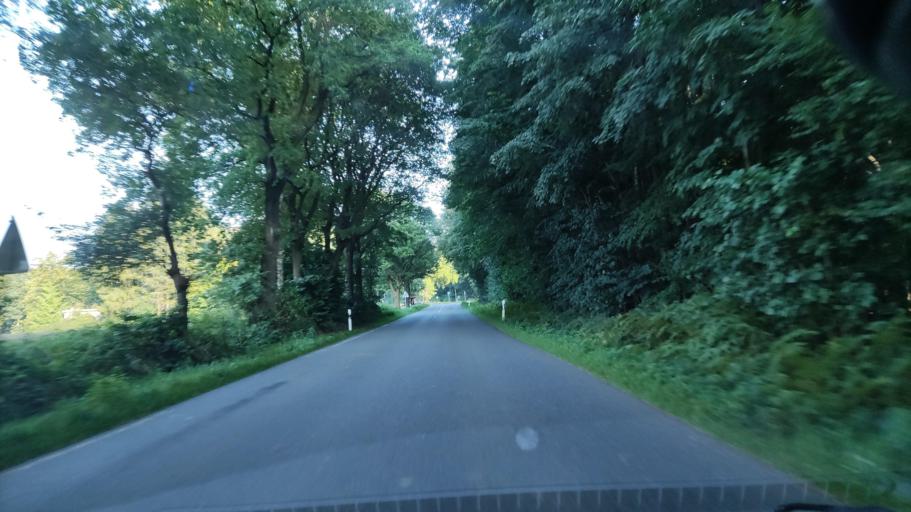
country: DE
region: Schleswig-Holstein
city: Kattendorf
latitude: 53.8663
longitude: 10.0237
